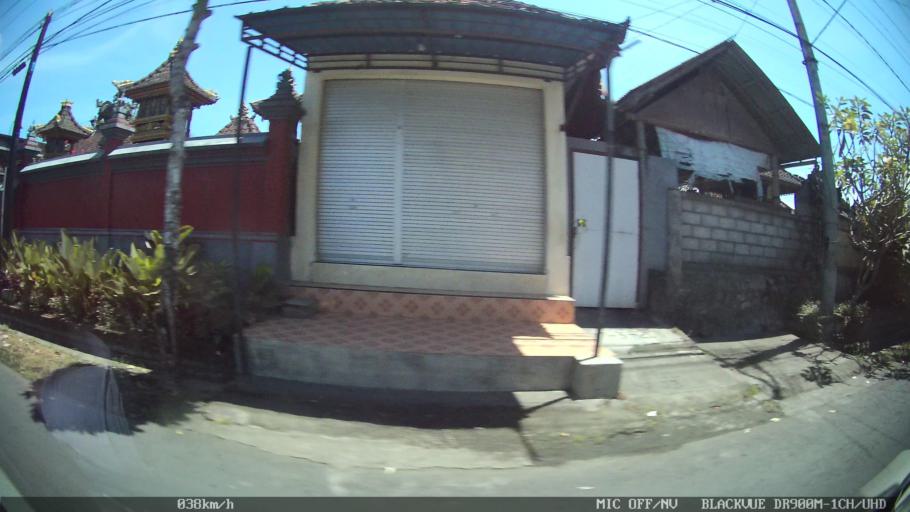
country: ID
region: Bali
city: Banjar Pasekan
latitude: -8.5739
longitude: 115.3226
